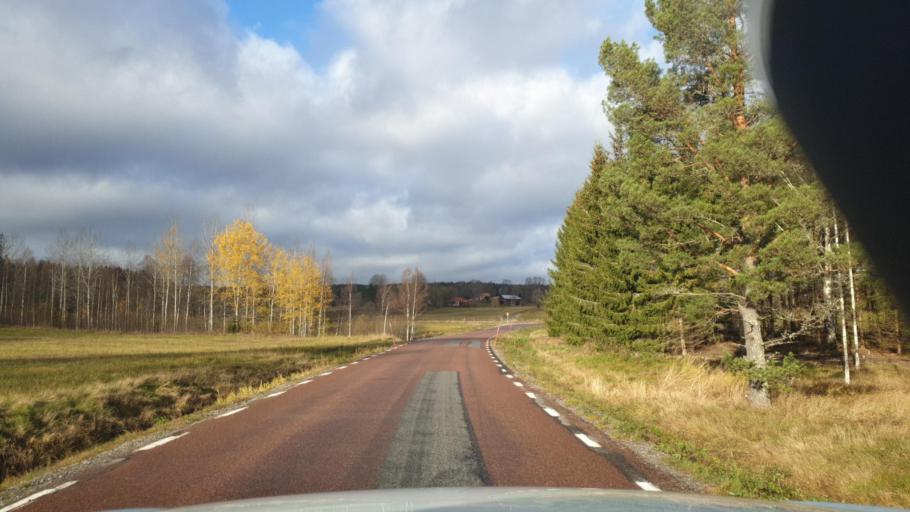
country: SE
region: Vaermland
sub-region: Grums Kommun
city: Slottsbron
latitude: 59.4593
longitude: 12.8791
